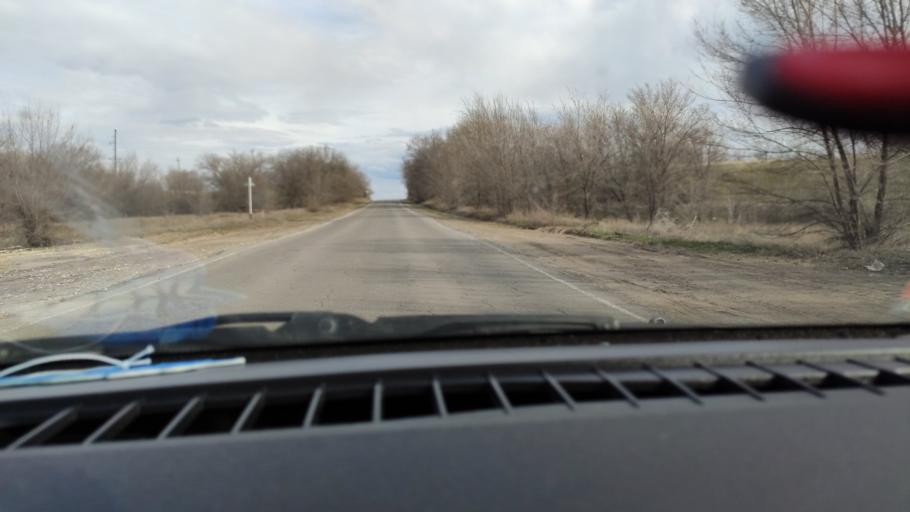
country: RU
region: Saratov
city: Krasnoarmeysk
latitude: 51.0784
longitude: 45.9708
